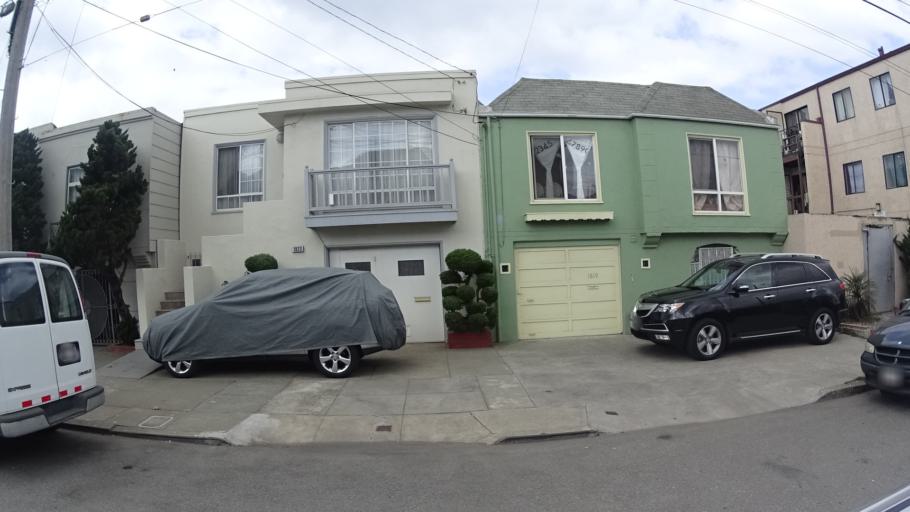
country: US
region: California
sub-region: San Mateo County
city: Daly City
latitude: 37.7526
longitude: -122.5075
